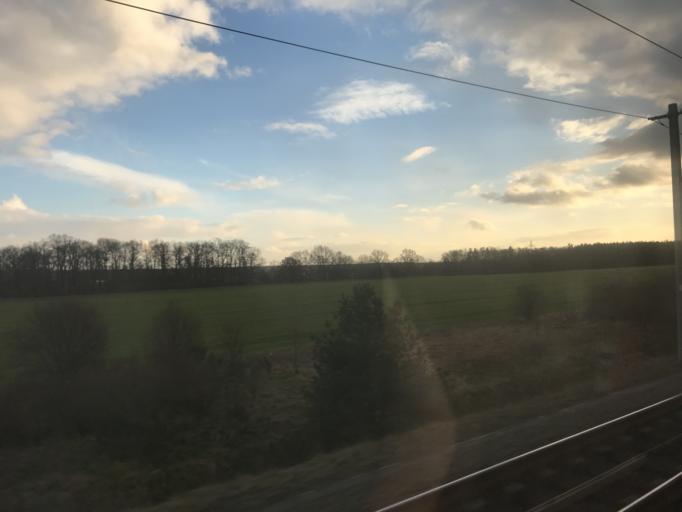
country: DE
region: Saxony-Anhalt
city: Uchtspringe
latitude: 52.5537
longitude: 11.6193
